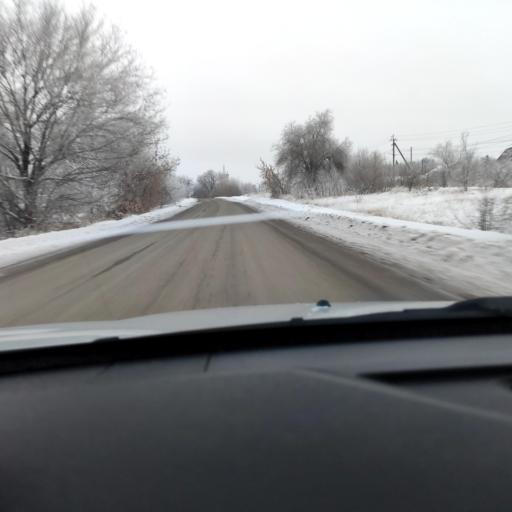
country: RU
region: Samara
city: Smyshlyayevka
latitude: 53.2444
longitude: 50.4814
